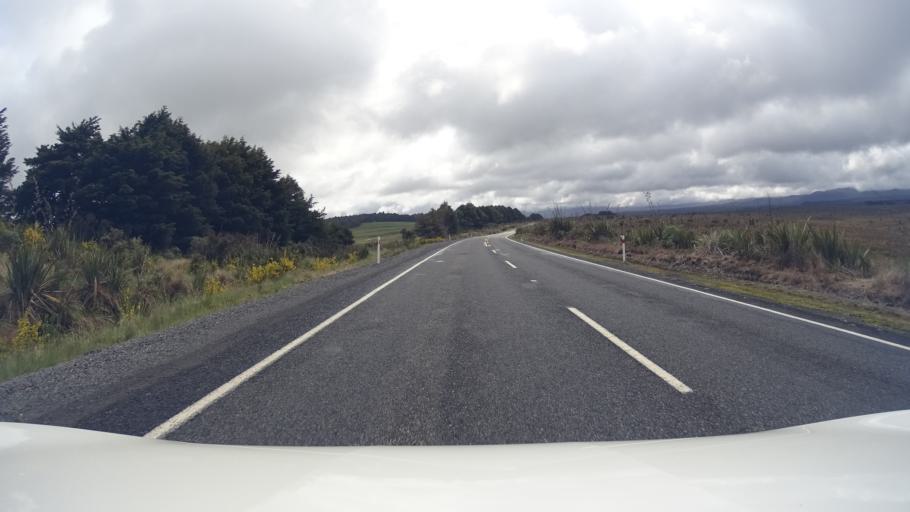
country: NZ
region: Manawatu-Wanganui
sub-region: Ruapehu District
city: Waiouru
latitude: -39.1806
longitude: 175.4473
